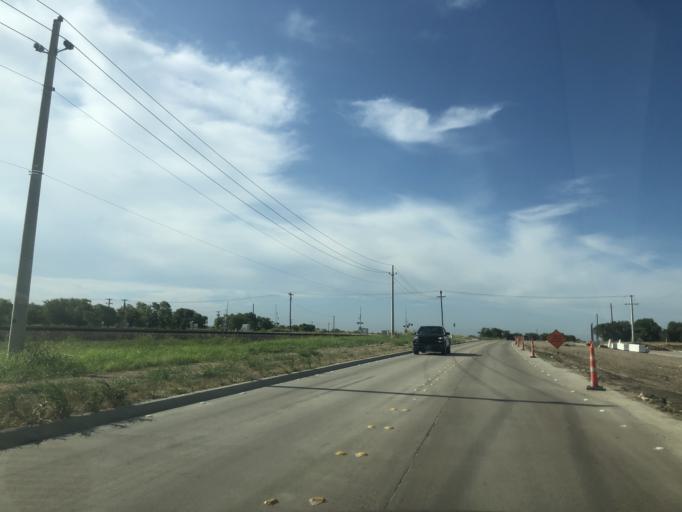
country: US
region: Texas
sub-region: Denton County
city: Justin
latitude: 33.0696
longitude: -97.2955
